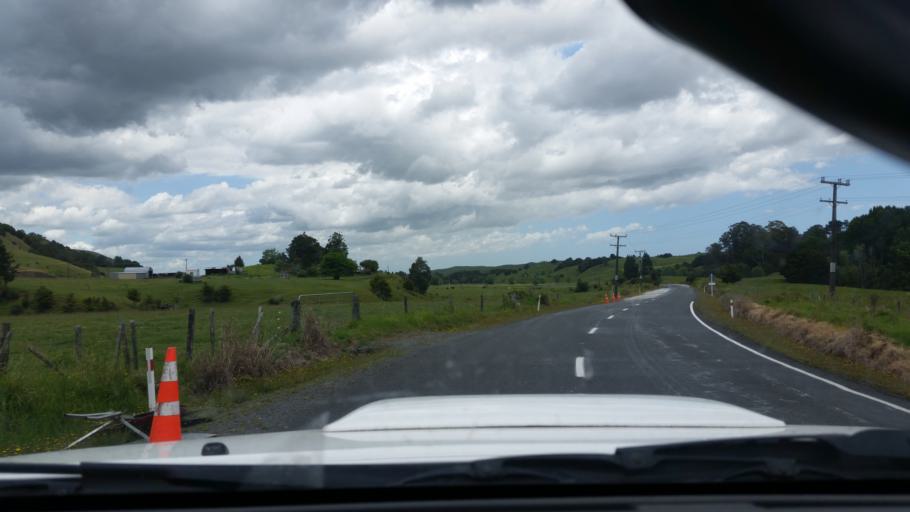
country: NZ
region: Northland
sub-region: Kaipara District
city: Dargaville
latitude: -35.7969
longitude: 173.9182
